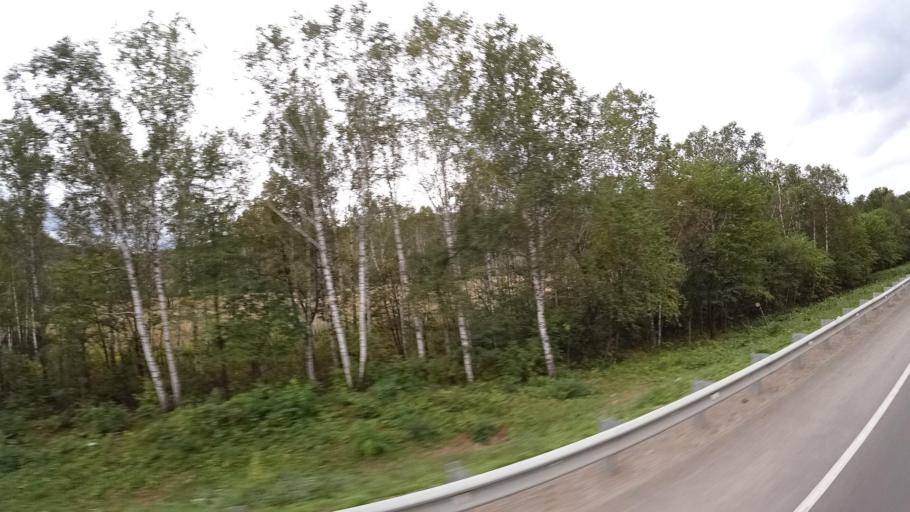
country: RU
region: Jewish Autonomous Oblast
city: Khingansk
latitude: 48.9844
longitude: 131.1440
